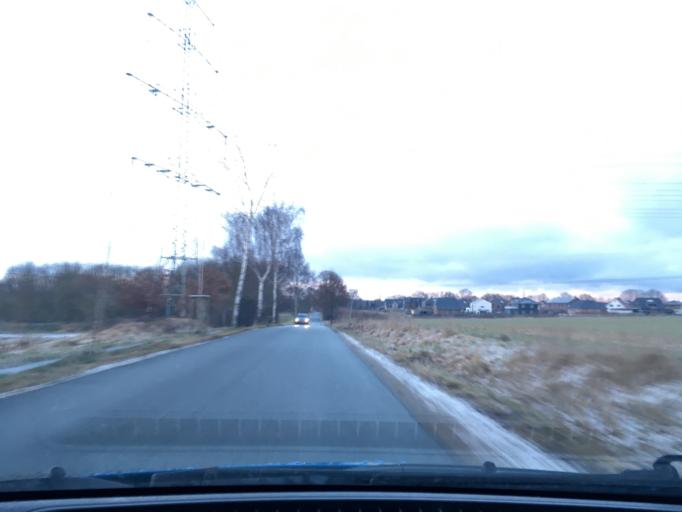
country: DE
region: Lower Saxony
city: Reppenstedt
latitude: 53.2232
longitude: 10.3659
